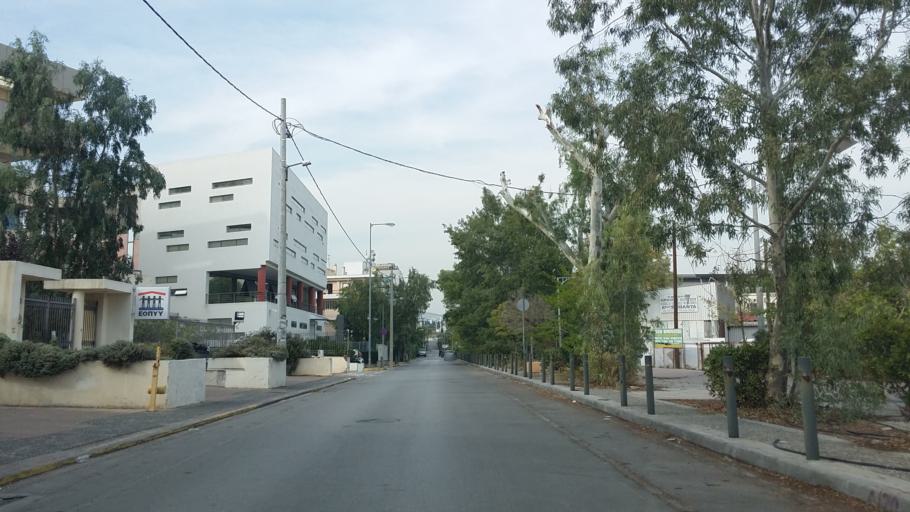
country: GR
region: Attica
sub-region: Nomarchia Athinas
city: Filothei
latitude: 38.0314
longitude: 23.7906
